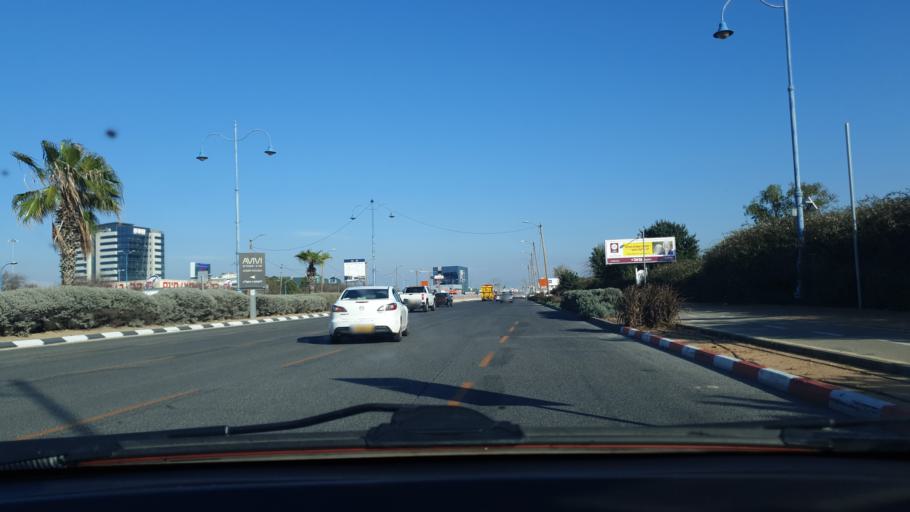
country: IL
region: Tel Aviv
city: Holon
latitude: 31.9869
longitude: 34.7587
